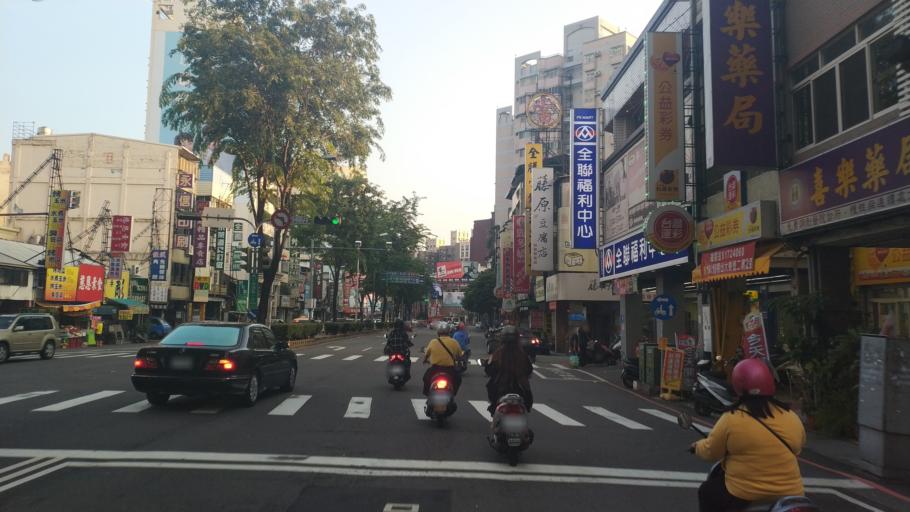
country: TW
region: Taiwan
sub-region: Taichung City
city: Taichung
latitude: 24.1530
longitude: 120.6773
